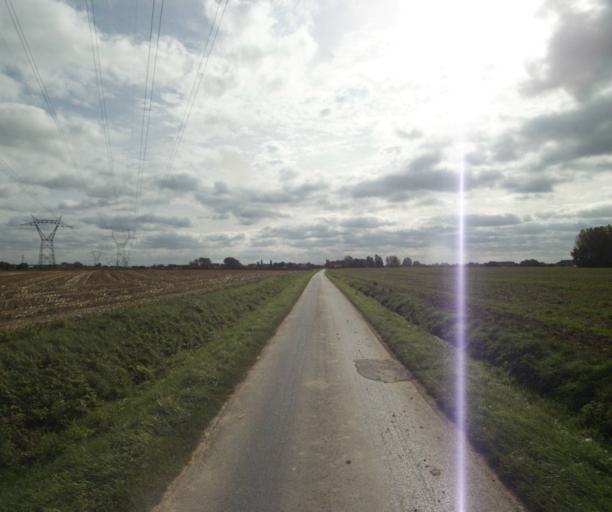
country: FR
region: Nord-Pas-de-Calais
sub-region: Departement du Nord
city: Bois-Grenier
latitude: 50.6582
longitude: 2.8620
